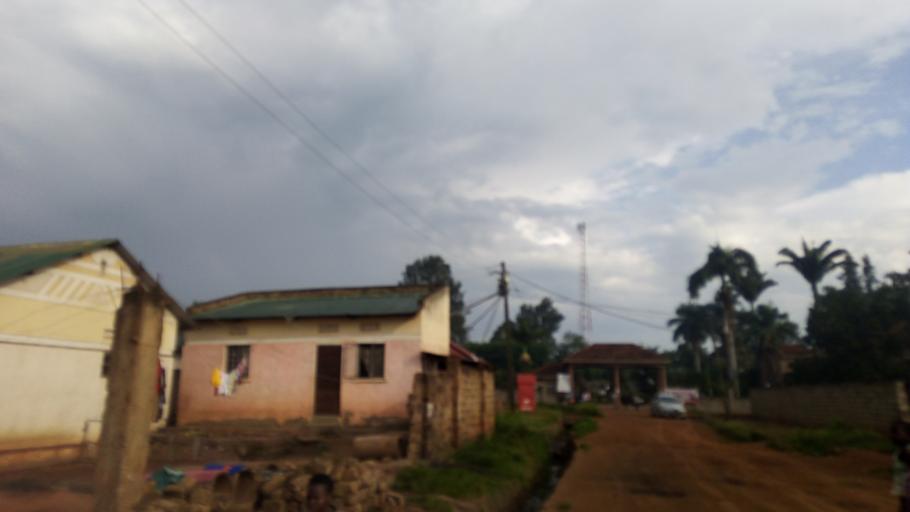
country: UG
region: Eastern Region
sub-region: Mbale District
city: Mbale
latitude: 1.0731
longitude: 34.1666
